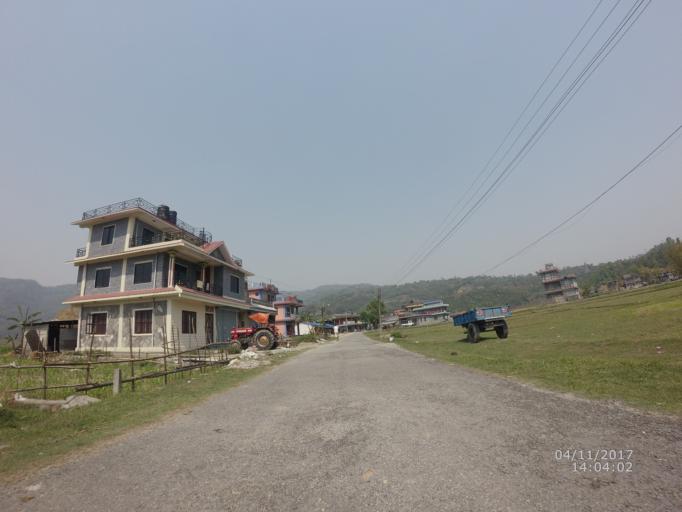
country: NP
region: Western Region
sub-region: Gandaki Zone
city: Pokhara
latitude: 28.1869
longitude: 84.0516
